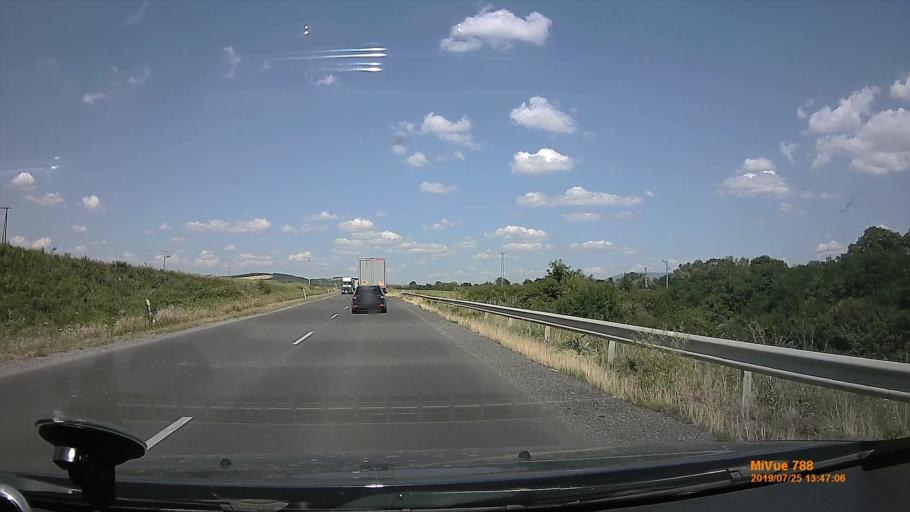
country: HU
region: Borsod-Abauj-Zemplen
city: Gonc
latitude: 48.4936
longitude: 21.2174
